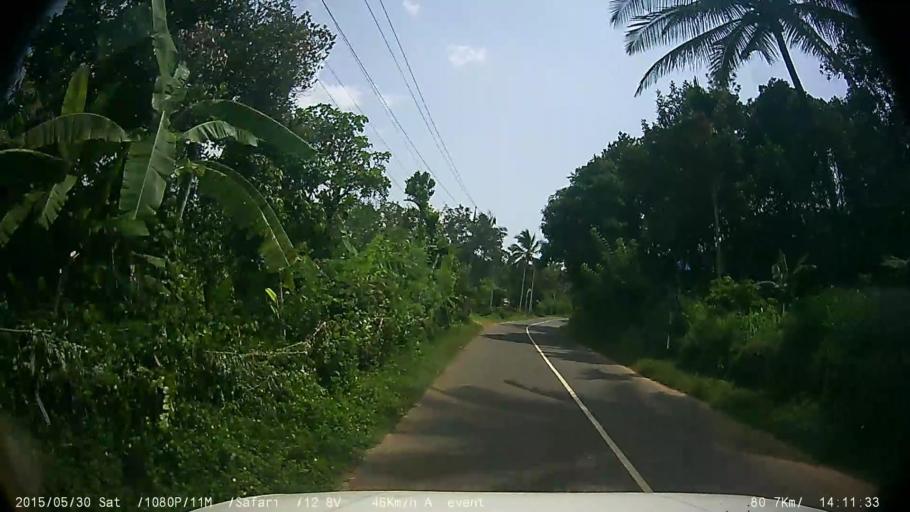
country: IN
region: Kerala
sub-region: Wayanad
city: Panamaram
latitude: 11.7911
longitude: 76.0536
